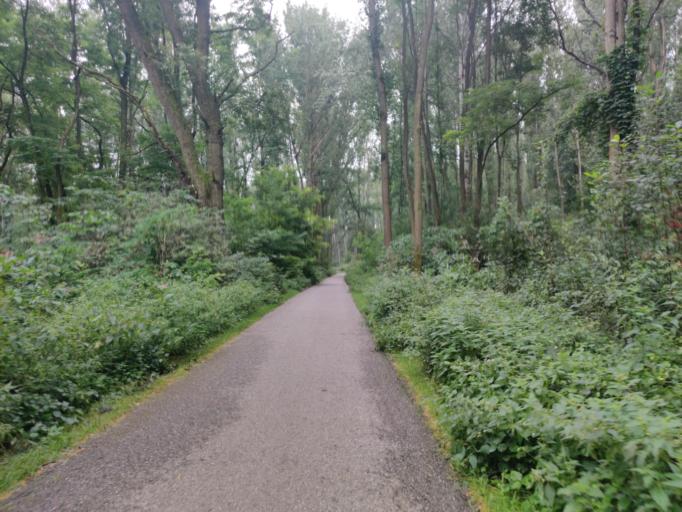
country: AT
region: Lower Austria
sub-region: Politischer Bezirk Krems
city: Gedersdorf
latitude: 48.3909
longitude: 15.6914
